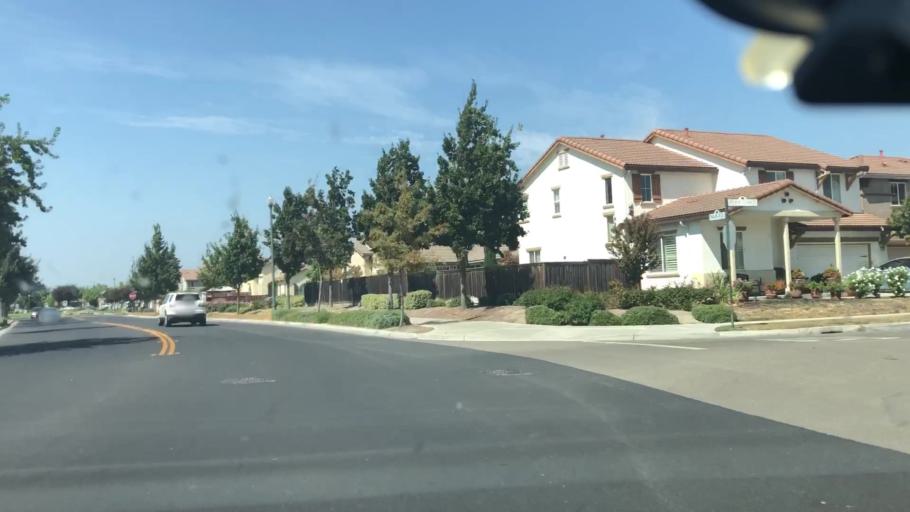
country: US
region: California
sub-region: San Joaquin County
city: Lathrop
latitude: 37.8136
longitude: -121.3070
